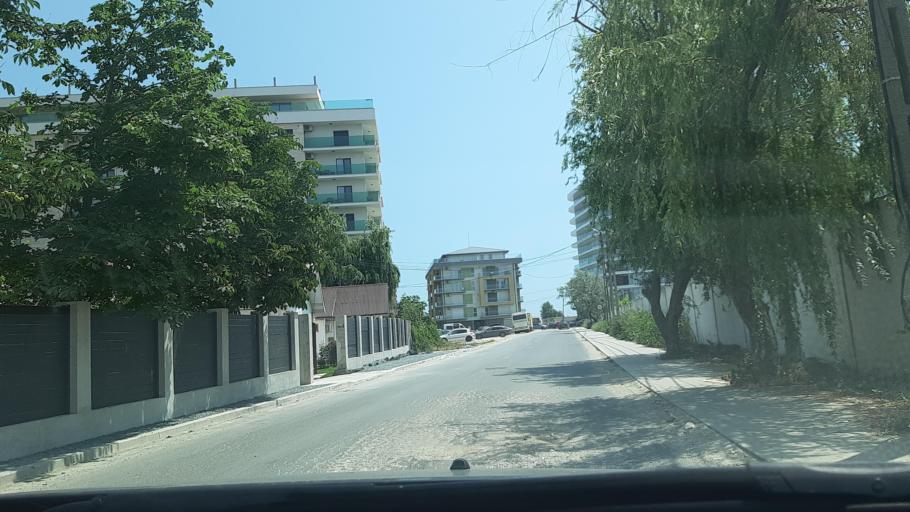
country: RO
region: Constanta
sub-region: Comuna Navodari
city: Navodari
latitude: 44.2888
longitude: 28.6198
